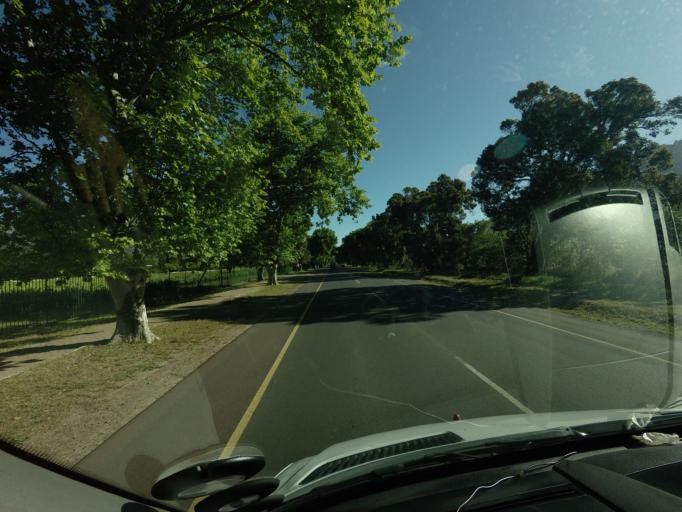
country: ZA
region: Western Cape
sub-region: Cape Winelands District Municipality
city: Stellenbosch
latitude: -33.8719
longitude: 18.9749
